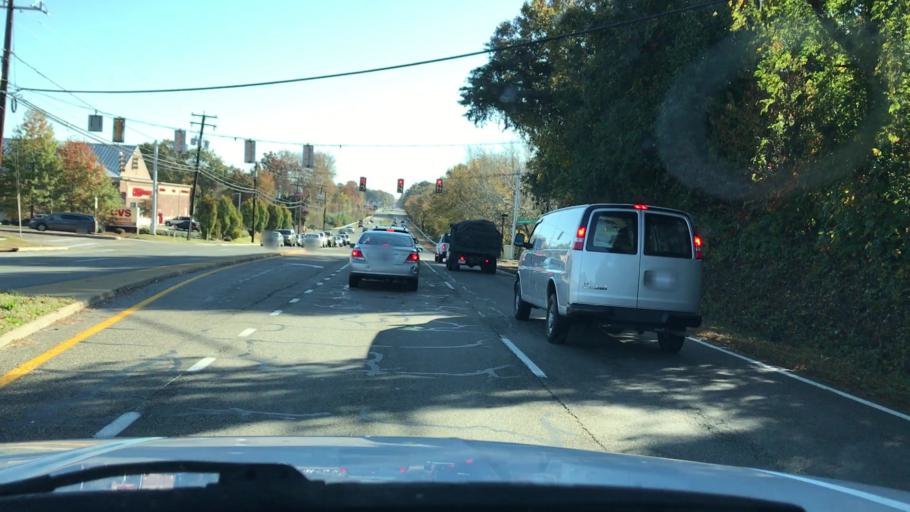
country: US
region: Virginia
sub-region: Henrico County
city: Short Pump
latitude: 37.5975
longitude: -77.6184
